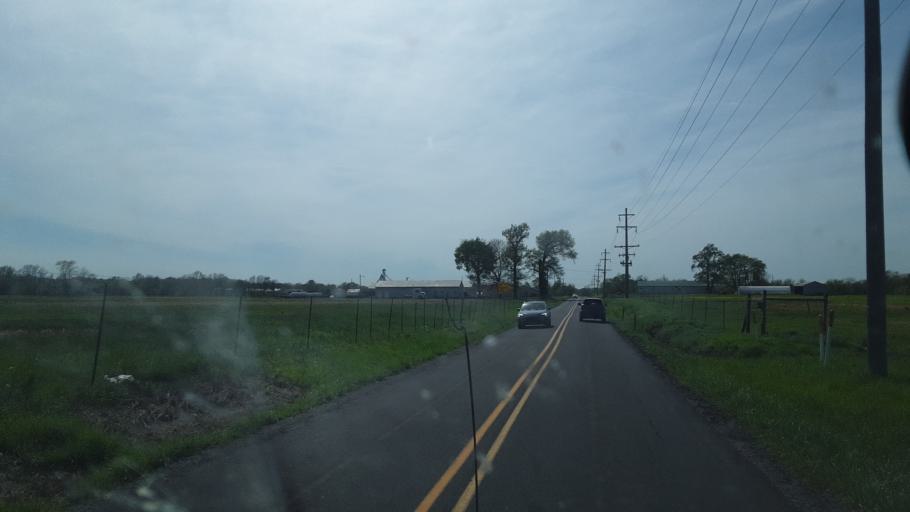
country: US
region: Illinois
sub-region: Jackson County
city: Carbondale
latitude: 37.7009
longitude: -89.2397
